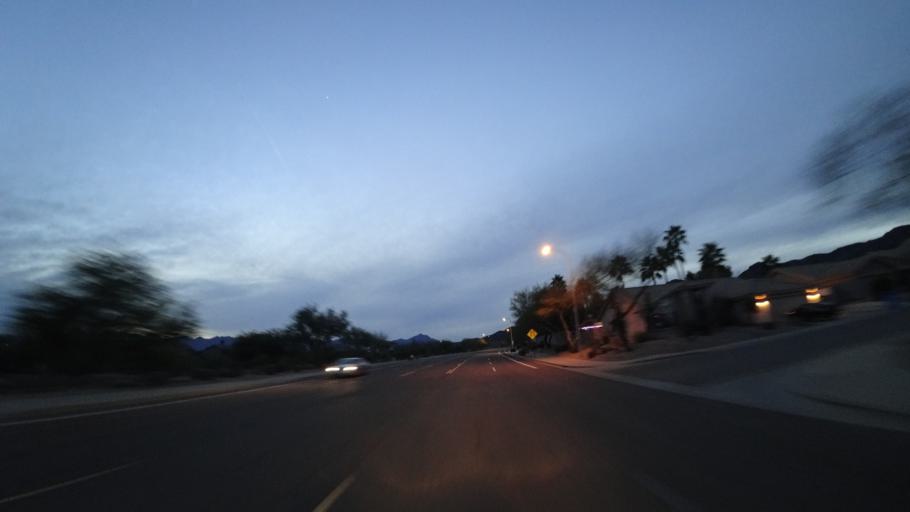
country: US
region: Arizona
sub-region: Maricopa County
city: Laveen
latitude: 33.3024
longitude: -112.0919
